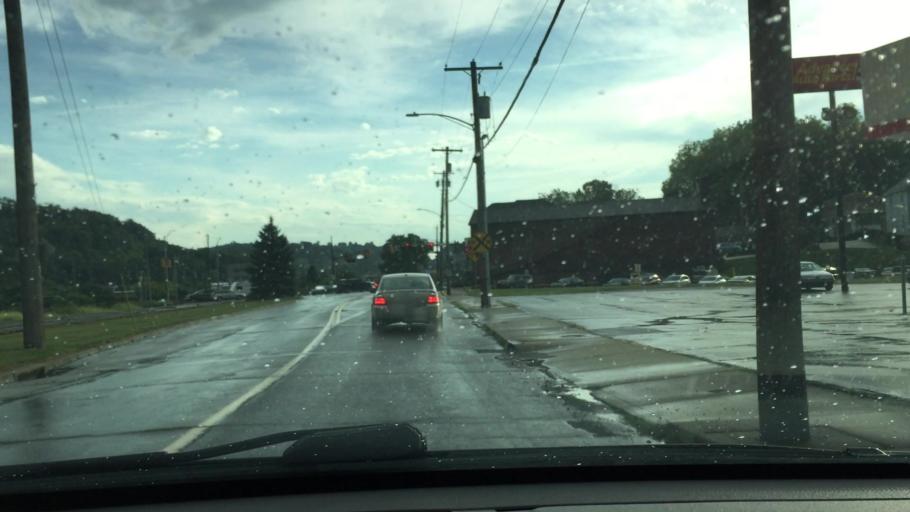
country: US
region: Pennsylvania
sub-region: Washington County
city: Canonsburg
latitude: 40.2632
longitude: -80.1758
